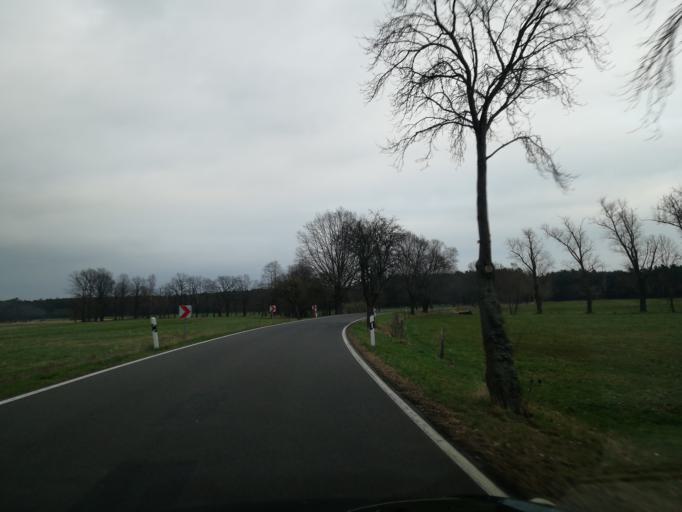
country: DE
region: Brandenburg
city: Vetschau
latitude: 51.7341
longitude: 14.1230
